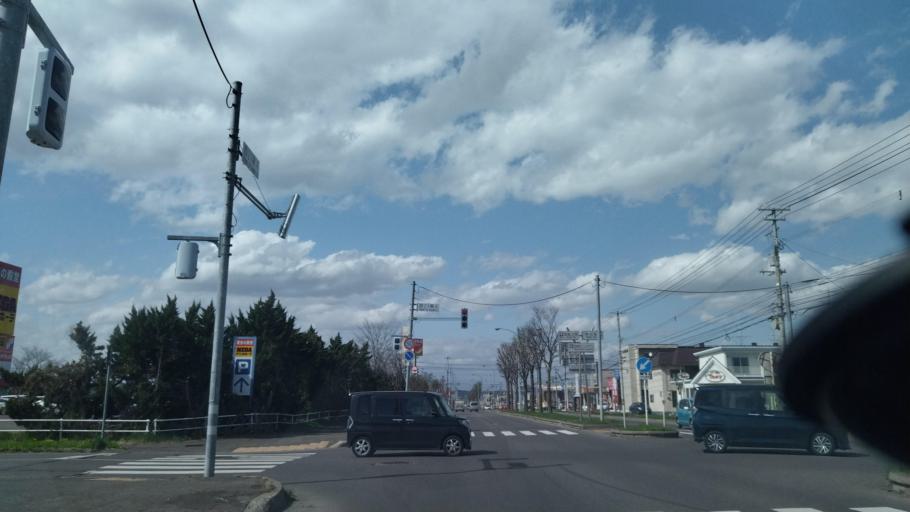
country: JP
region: Hokkaido
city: Obihiro
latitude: 42.9110
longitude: 143.1453
